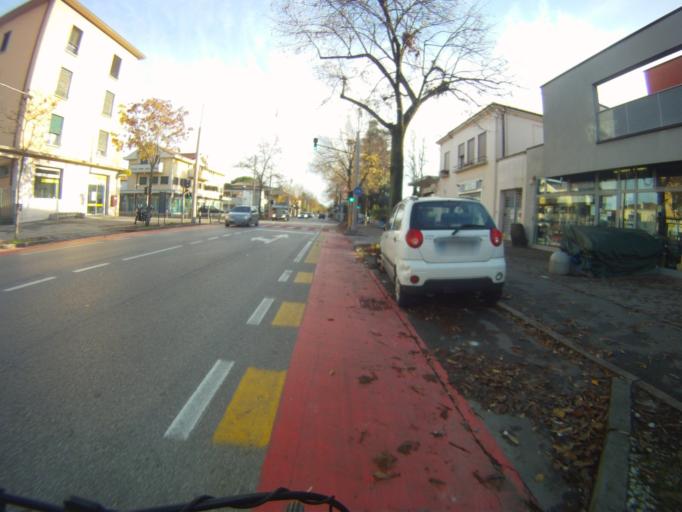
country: IT
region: Veneto
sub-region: Provincia di Padova
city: Padova
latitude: 45.3916
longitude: 11.8923
